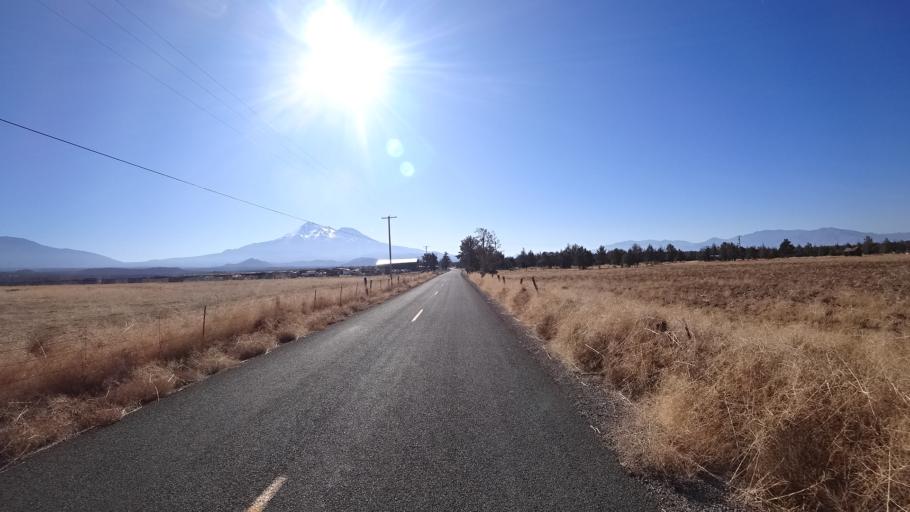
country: US
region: California
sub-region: Siskiyou County
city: Weed
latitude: 41.5955
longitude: -122.3019
